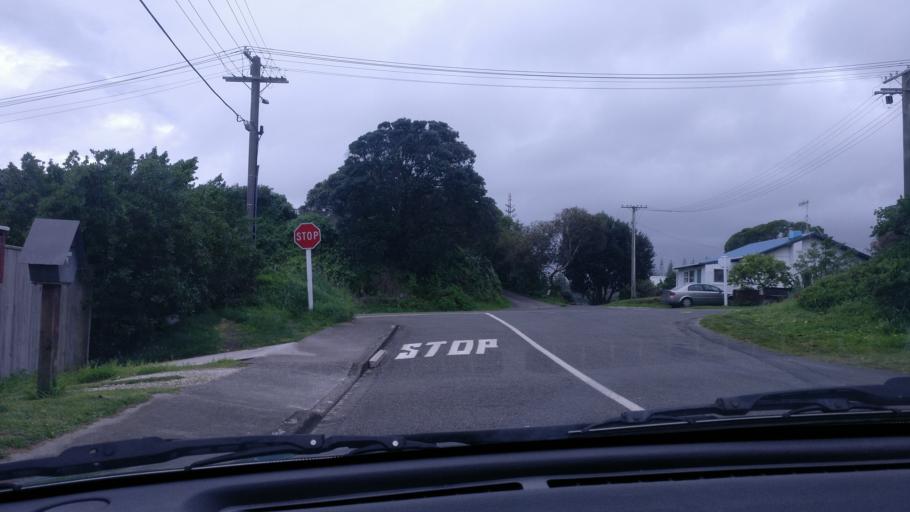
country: NZ
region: Wellington
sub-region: Kapiti Coast District
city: Paraparaumu
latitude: -40.9762
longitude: 174.9592
